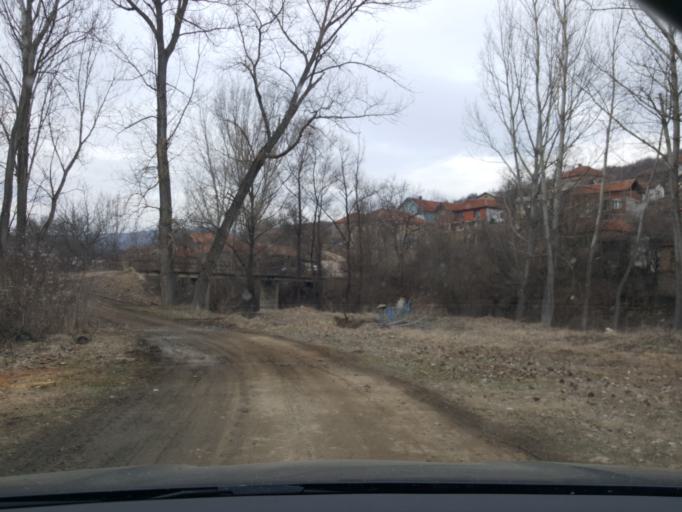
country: RS
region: Central Serbia
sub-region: Pirotski Okrug
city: Dimitrovgrad
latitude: 43.0013
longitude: 22.7640
